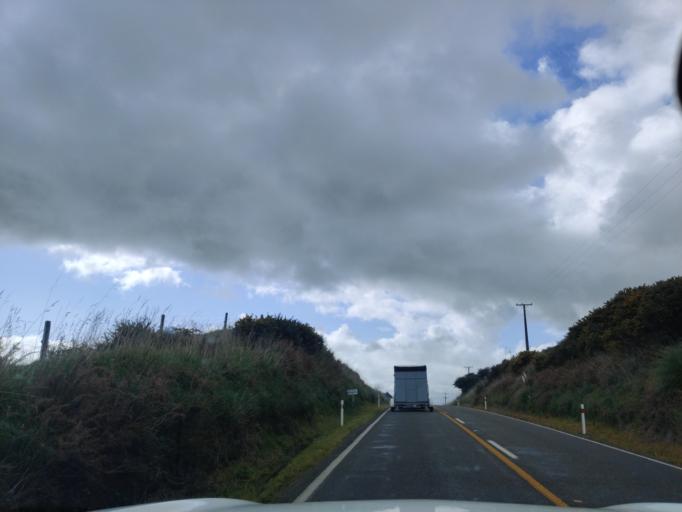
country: NZ
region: Manawatu-Wanganui
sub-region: Palmerston North City
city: Palmerston North
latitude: -40.4442
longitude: 175.5501
